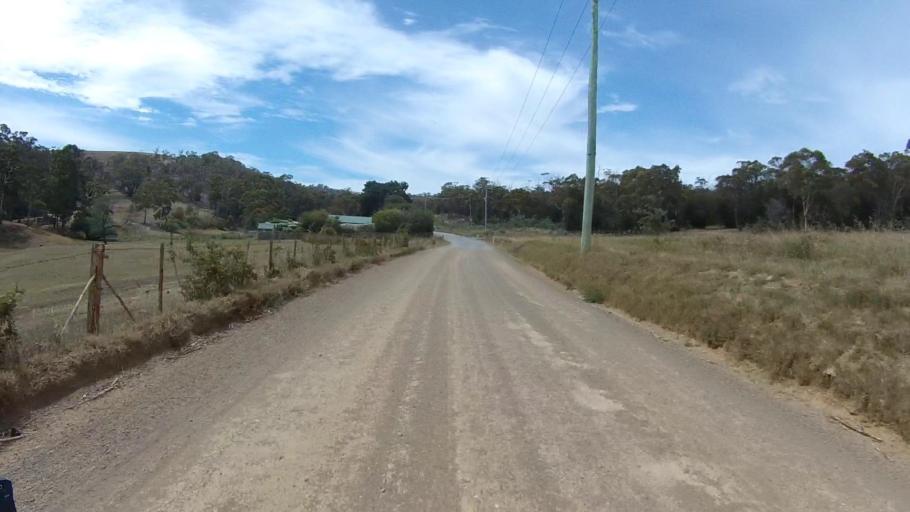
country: AU
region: Tasmania
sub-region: Sorell
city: Sorell
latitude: -42.8003
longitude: 147.6513
